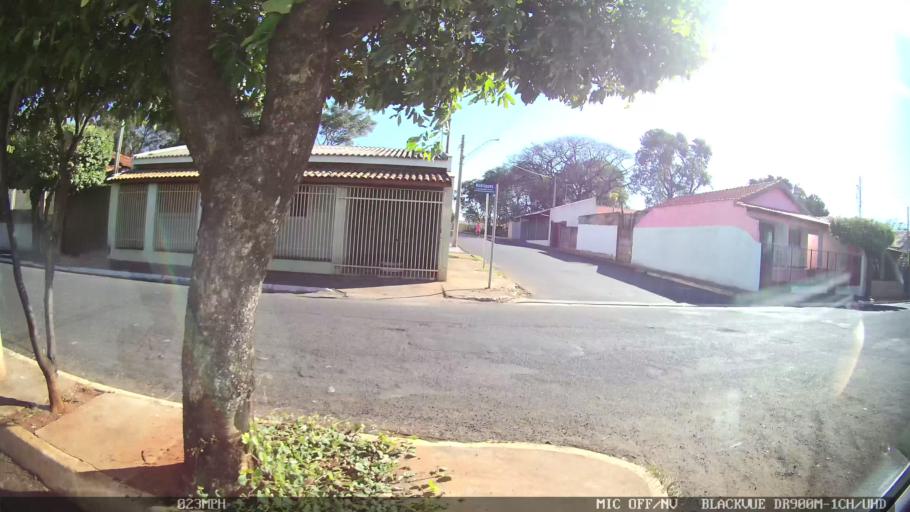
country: BR
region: Sao Paulo
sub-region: Olimpia
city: Olimpia
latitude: -20.7500
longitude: -48.9086
